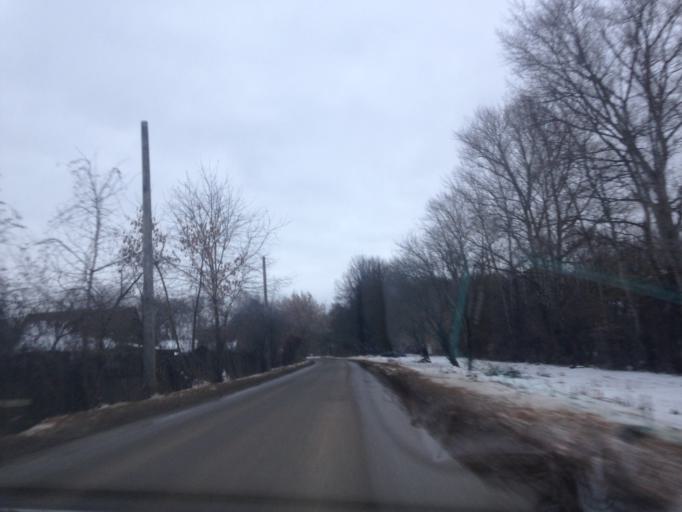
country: RU
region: Tula
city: Shchekino
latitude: 54.0225
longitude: 37.5141
